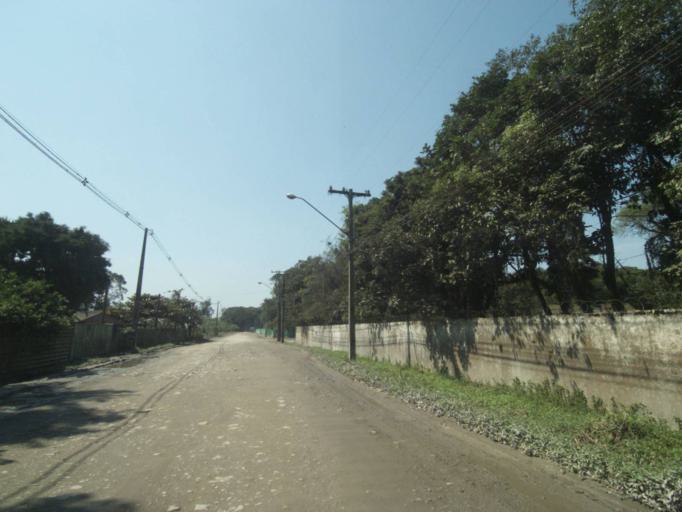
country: BR
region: Parana
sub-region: Paranagua
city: Paranagua
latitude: -25.5481
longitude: -48.5762
